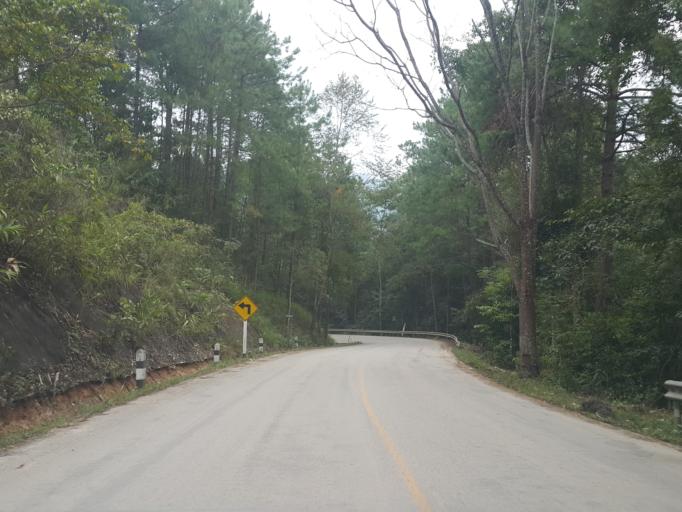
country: TH
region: Mae Hong Son
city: Mae Hi
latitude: 19.2519
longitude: 98.6491
